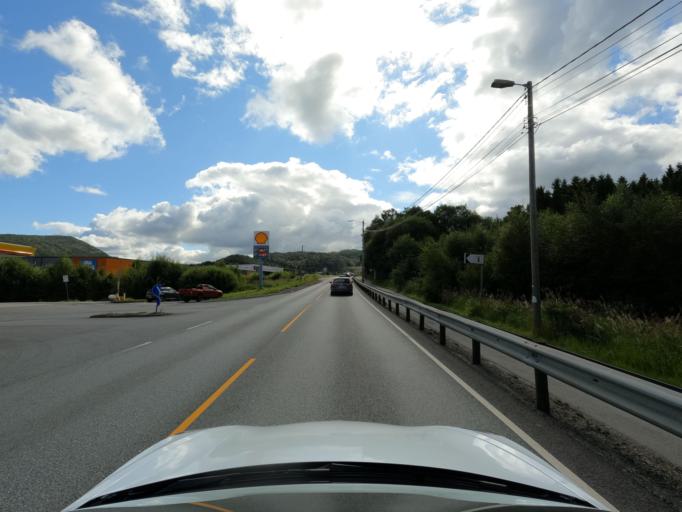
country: NO
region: Hordaland
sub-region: Bergen
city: Hylkje
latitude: 60.4887
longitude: 5.3767
